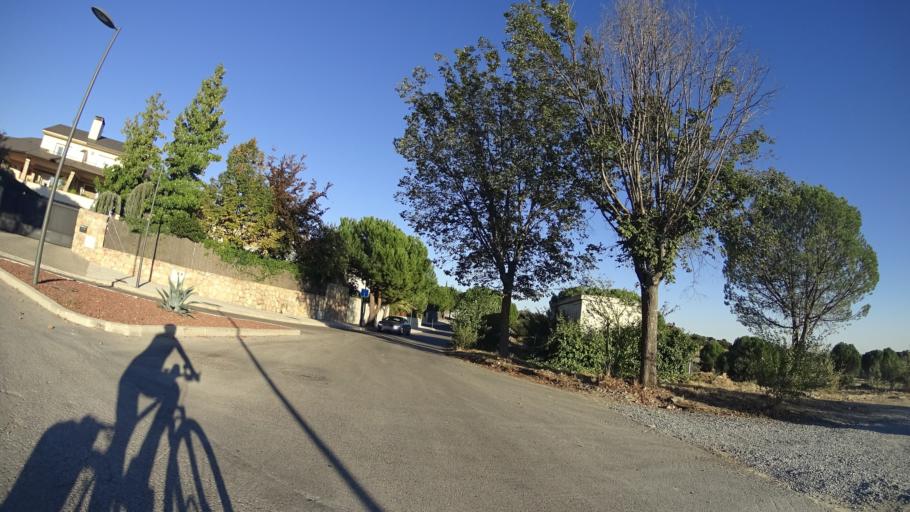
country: ES
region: Madrid
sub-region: Provincia de Madrid
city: Torrelodones
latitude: 40.5719
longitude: -3.9379
